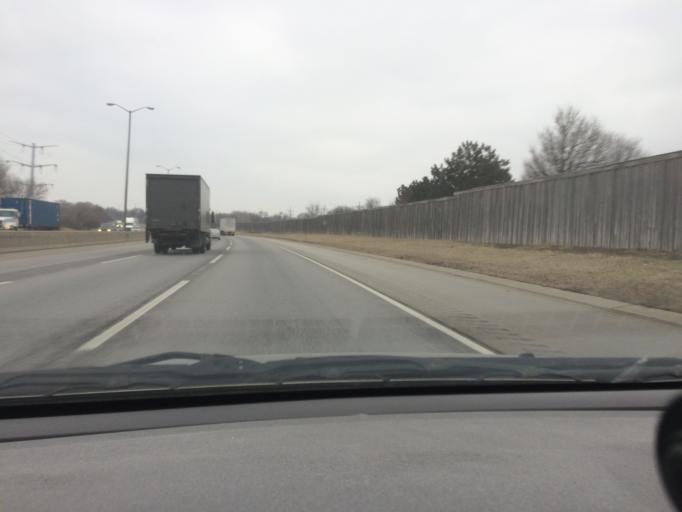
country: US
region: Illinois
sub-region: DuPage County
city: Lombard
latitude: 41.8749
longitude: -88.0338
